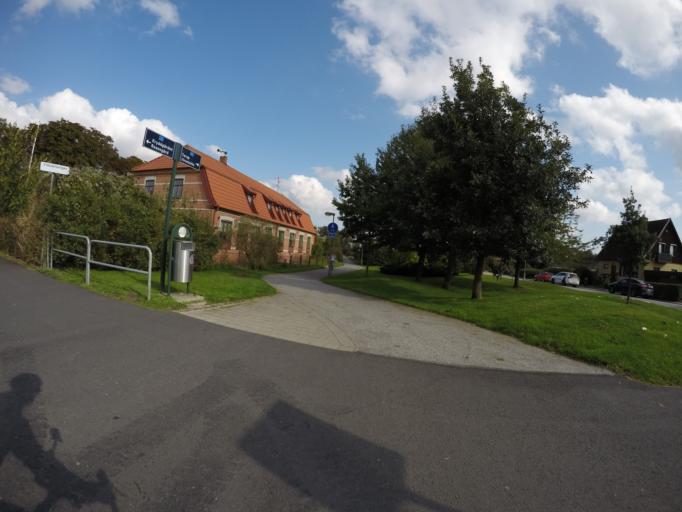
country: SE
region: Skane
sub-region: Burlovs Kommun
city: Arloev
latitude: 55.5894
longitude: 13.0614
